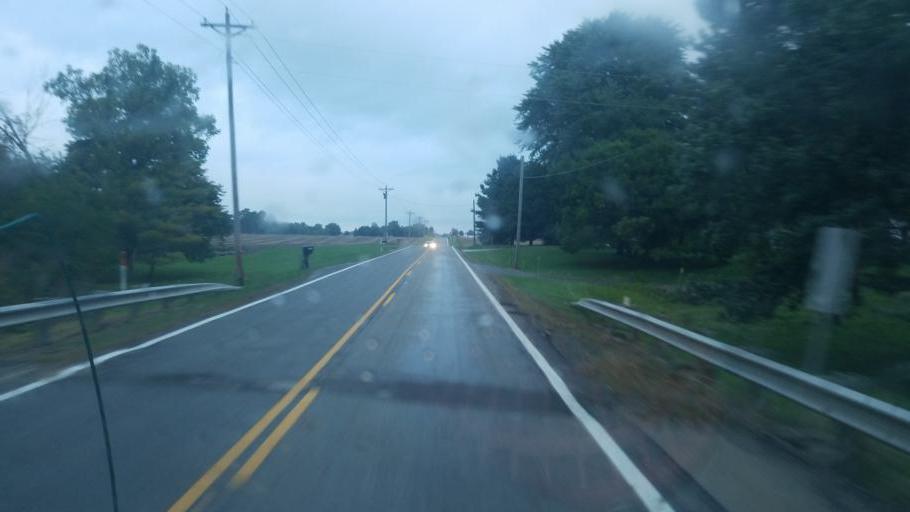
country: US
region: Ohio
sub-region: Morrow County
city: Cardington
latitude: 40.5810
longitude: -82.9622
